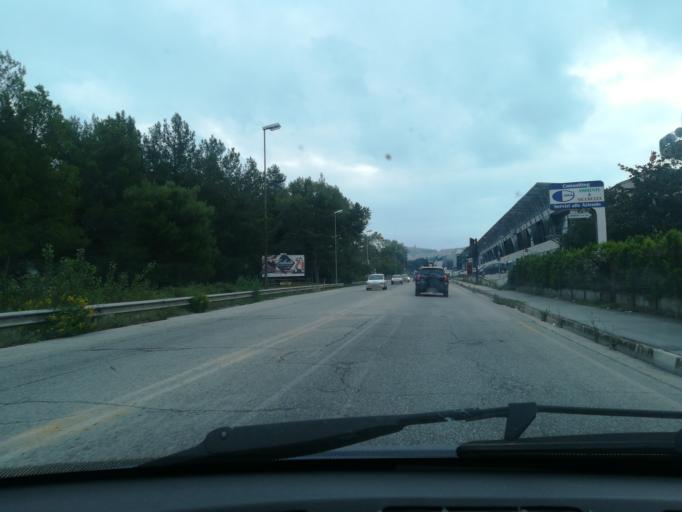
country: IT
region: The Marches
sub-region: Provincia di Macerata
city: Zona Industriale
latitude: 43.2678
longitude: 13.4865
